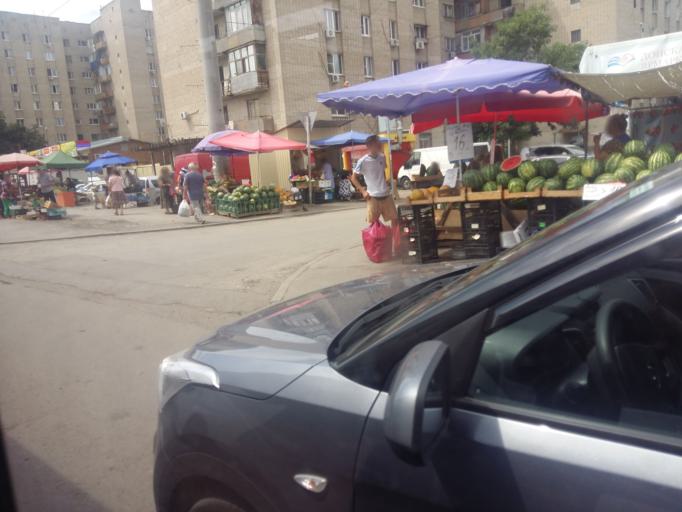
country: RU
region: Rostov
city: Imeni Chkalova
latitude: 47.2846
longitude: 39.7573
